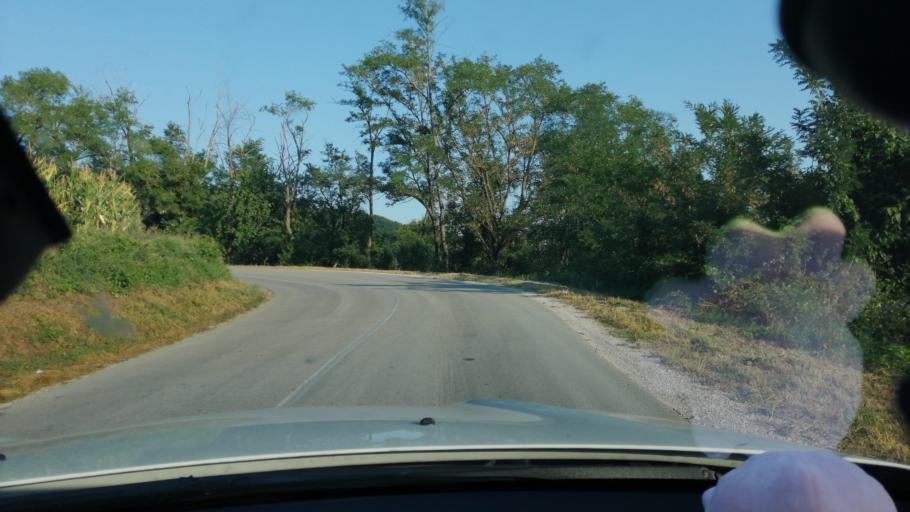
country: RS
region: Central Serbia
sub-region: Moravicki Okrug
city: Cacak
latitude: 43.8388
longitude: 20.2749
